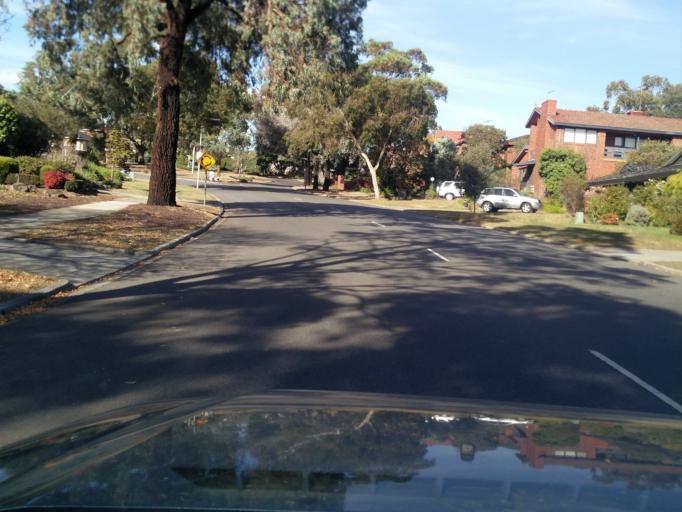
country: AU
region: Victoria
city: Macleod
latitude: -37.7333
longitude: 145.0701
